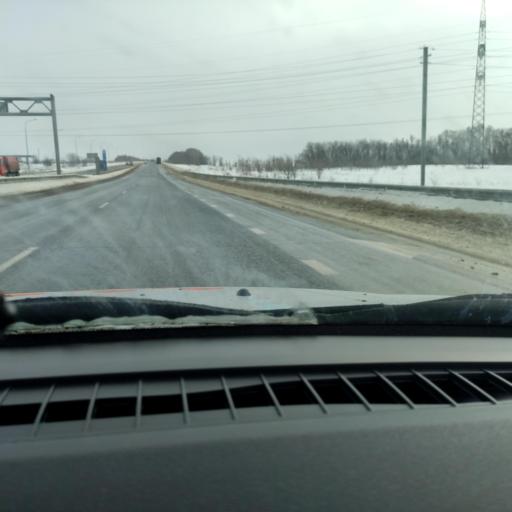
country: RU
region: Samara
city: Dubovyy Umet
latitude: 53.0132
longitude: 50.2385
